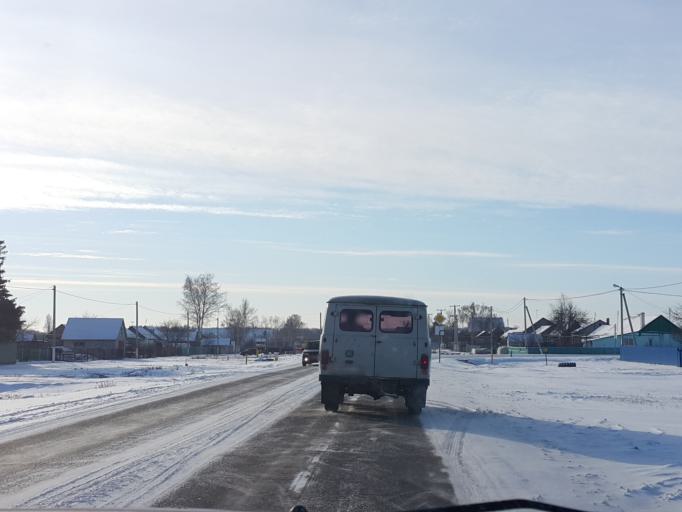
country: RU
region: Tambov
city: Znamenka
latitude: 52.4136
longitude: 41.4249
